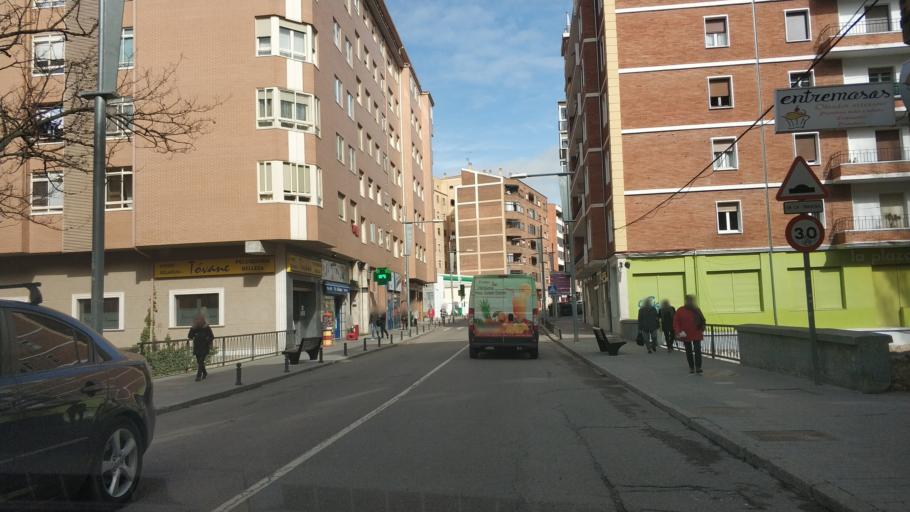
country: ES
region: Castille and Leon
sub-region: Provincia de Burgos
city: Aranda de Duero
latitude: 41.6741
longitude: -3.6858
